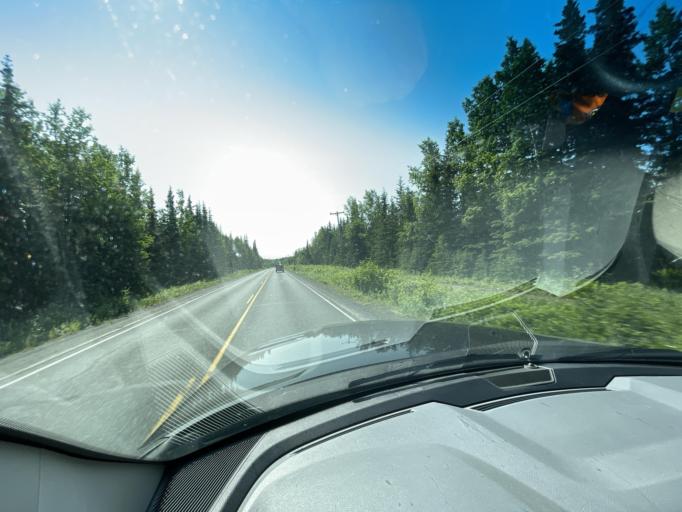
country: US
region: Alaska
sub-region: Kenai Peninsula Borough
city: Cohoe
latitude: 60.3048
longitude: -151.2867
